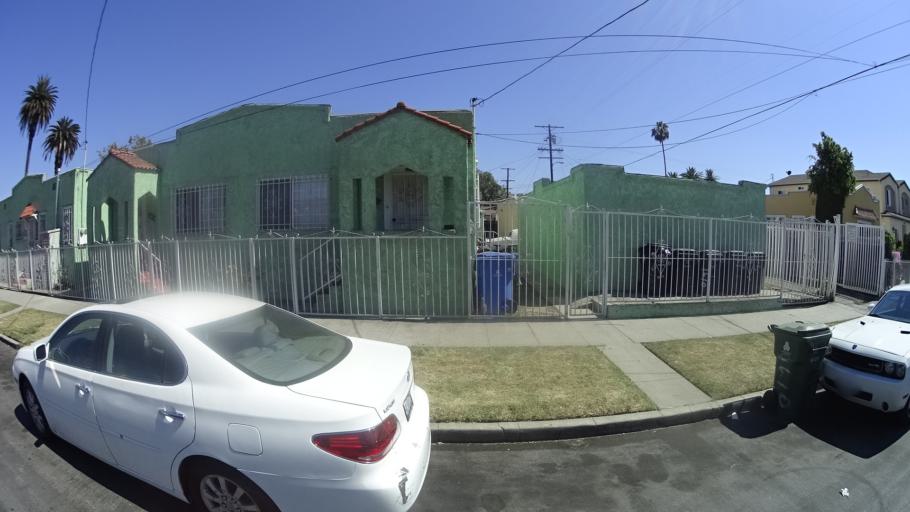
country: US
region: California
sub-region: Los Angeles County
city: View Park-Windsor Hills
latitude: 33.9905
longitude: -118.3050
